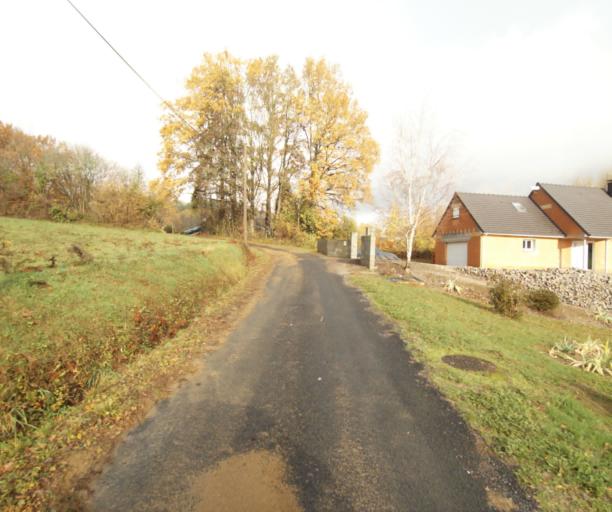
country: FR
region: Limousin
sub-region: Departement de la Correze
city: Cornil
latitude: 45.1985
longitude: 1.6517
